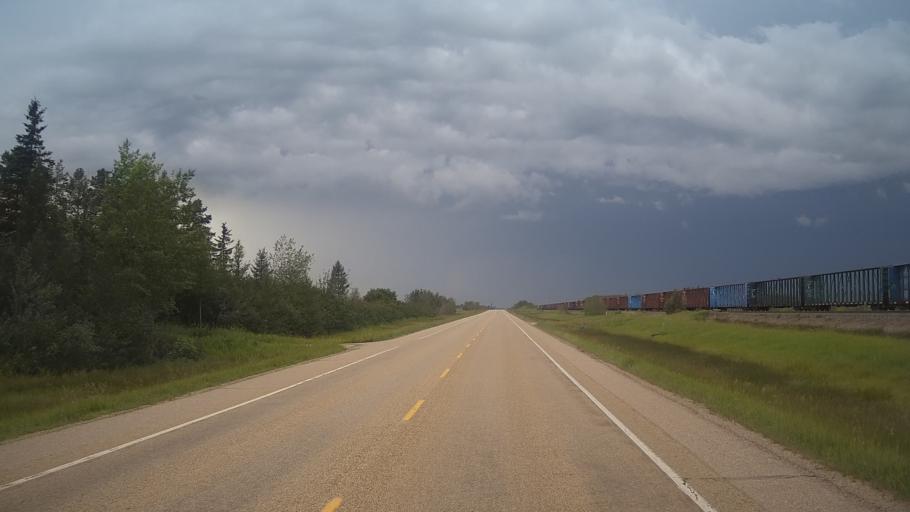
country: CA
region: Alberta
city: Tofield
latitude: 53.2717
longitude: -112.3761
